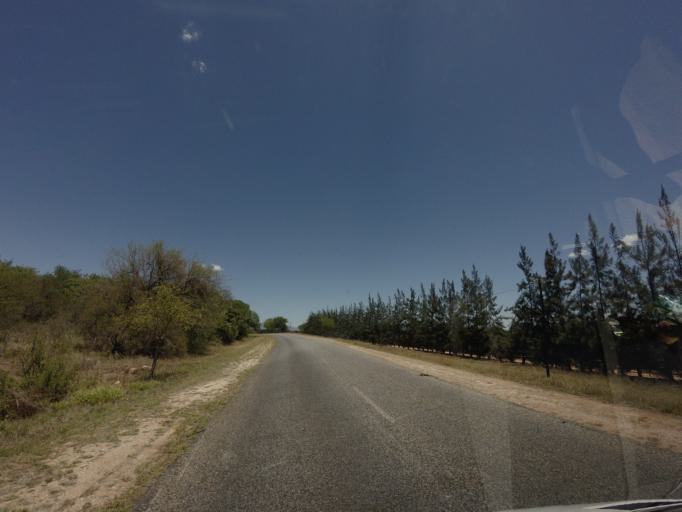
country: ZA
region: Limpopo
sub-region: Mopani District Municipality
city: Hoedspruit
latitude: -24.3698
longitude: 30.7205
